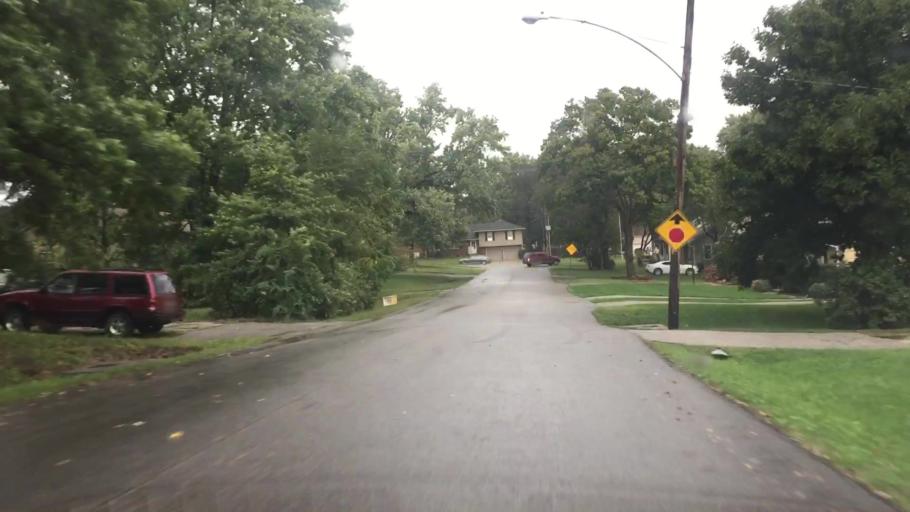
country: US
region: Kansas
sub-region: Johnson County
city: Shawnee
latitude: 39.0281
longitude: -94.7291
